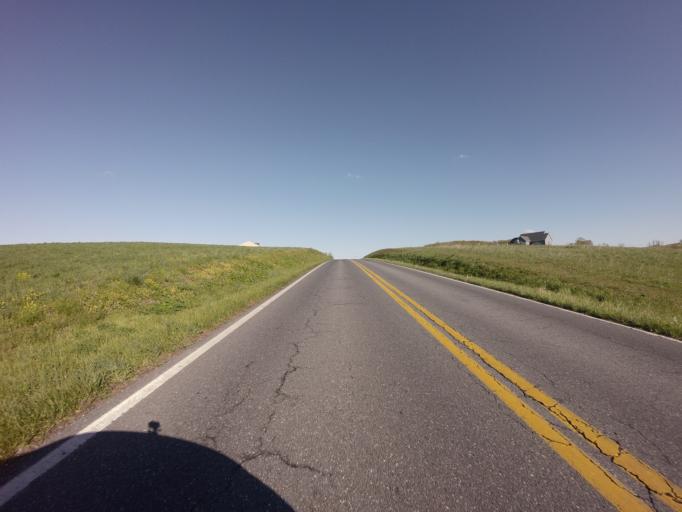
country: US
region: Maryland
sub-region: Frederick County
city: Woodsboro
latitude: 39.5701
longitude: -77.2504
